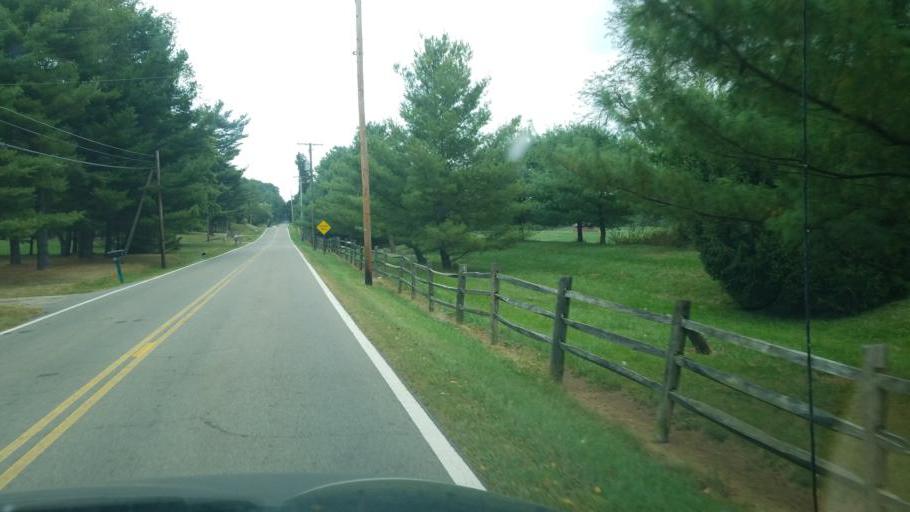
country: US
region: Ohio
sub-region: Licking County
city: Newark
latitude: 40.1000
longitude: -82.4568
